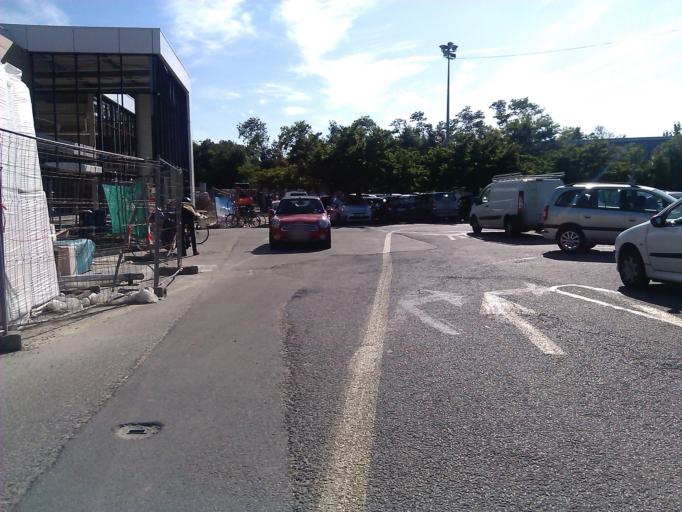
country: FR
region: Aquitaine
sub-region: Departement de la Gironde
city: Pessac
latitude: 44.8103
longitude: -0.6188
